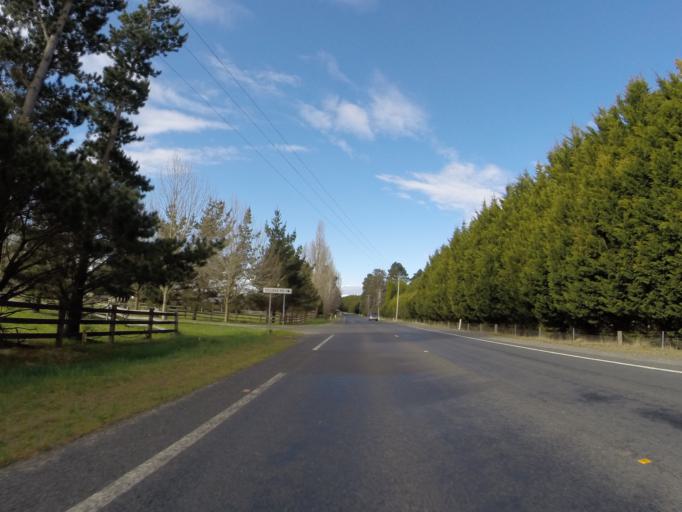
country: AU
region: New South Wales
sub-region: Wingecarribee
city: Moss Vale
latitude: -34.5791
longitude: 150.3049
